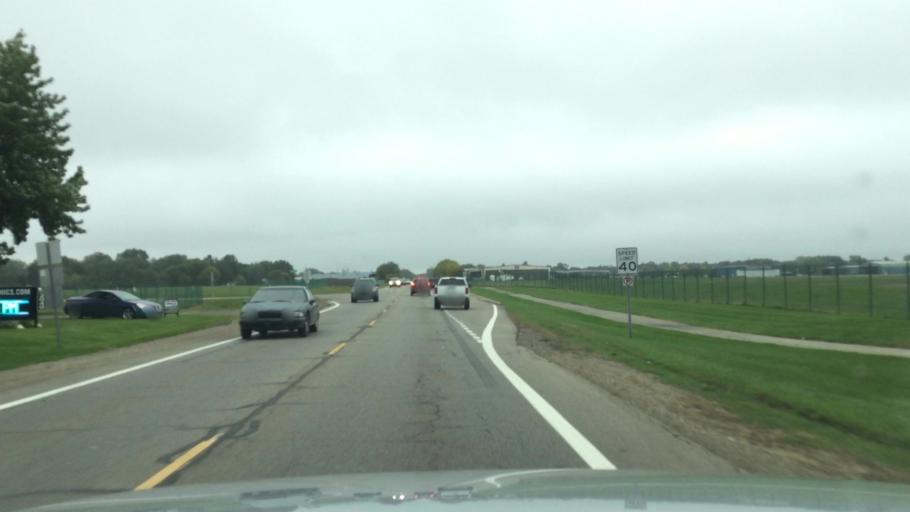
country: US
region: Michigan
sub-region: Oakland County
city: Waterford
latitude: 42.6682
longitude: -83.4064
